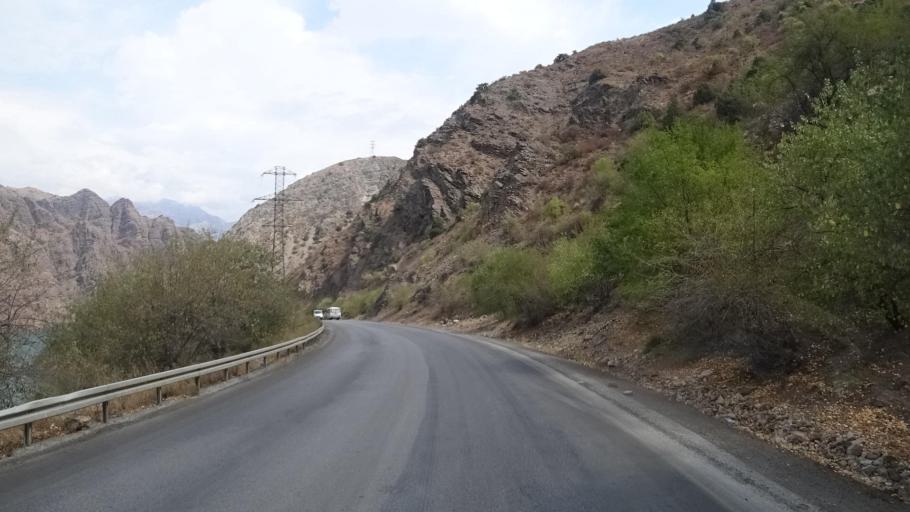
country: KG
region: Jalal-Abad
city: Tash-Kumyr
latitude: 41.5750
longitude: 72.5404
